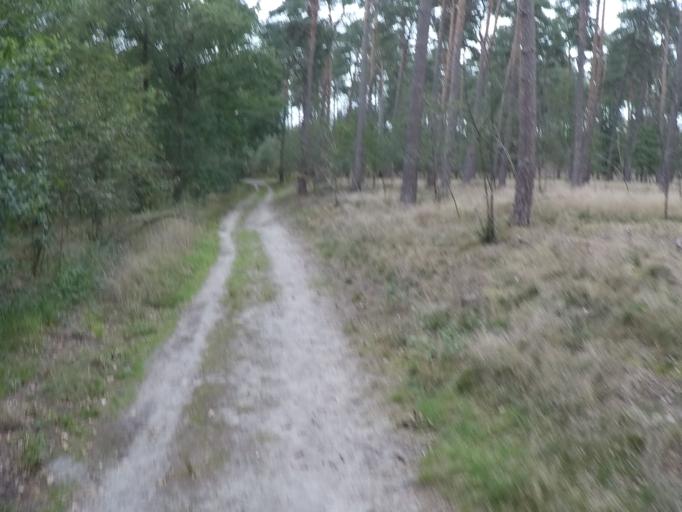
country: BE
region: Flanders
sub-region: Provincie Antwerpen
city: Herentals
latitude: 51.1950
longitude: 4.8648
